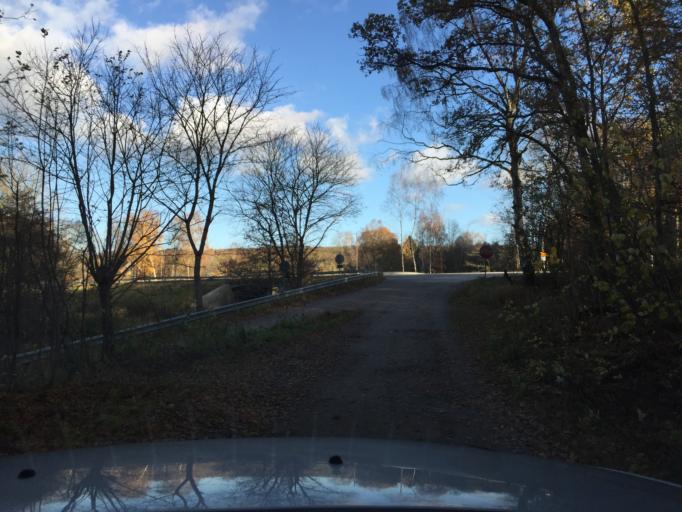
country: SE
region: Skane
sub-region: Hassleholms Kommun
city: Tormestorp
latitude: 56.0699
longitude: 13.7398
